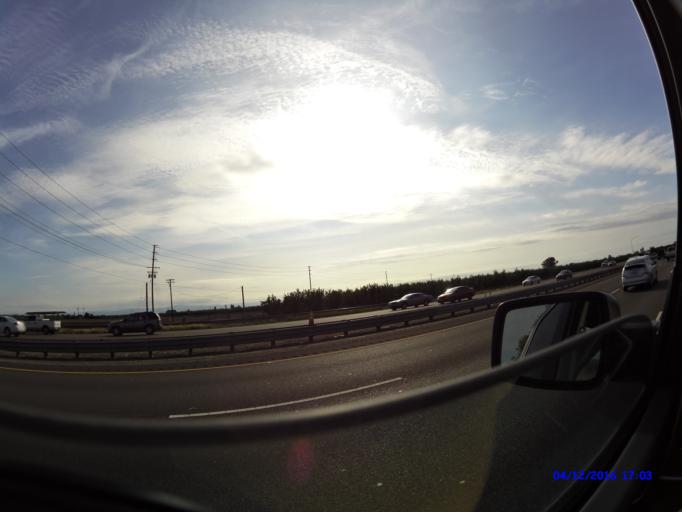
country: US
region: California
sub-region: Stanislaus County
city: Salida
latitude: 37.7208
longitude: -121.0983
